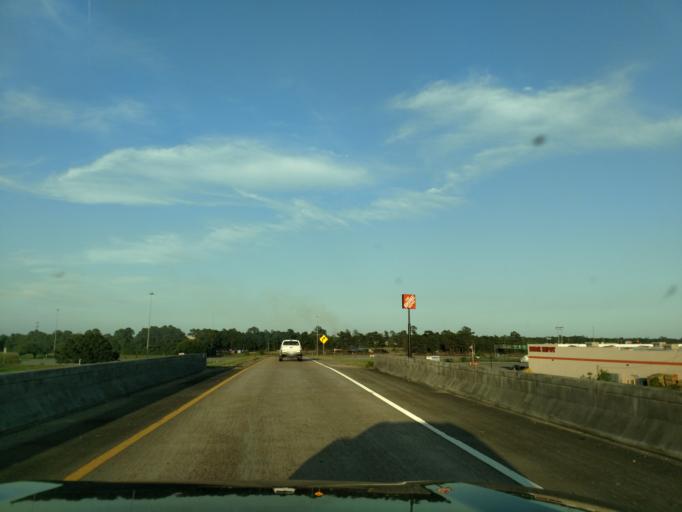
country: US
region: Mississippi
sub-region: Harrison County
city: West Gulfport
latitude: 30.4312
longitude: -89.0963
